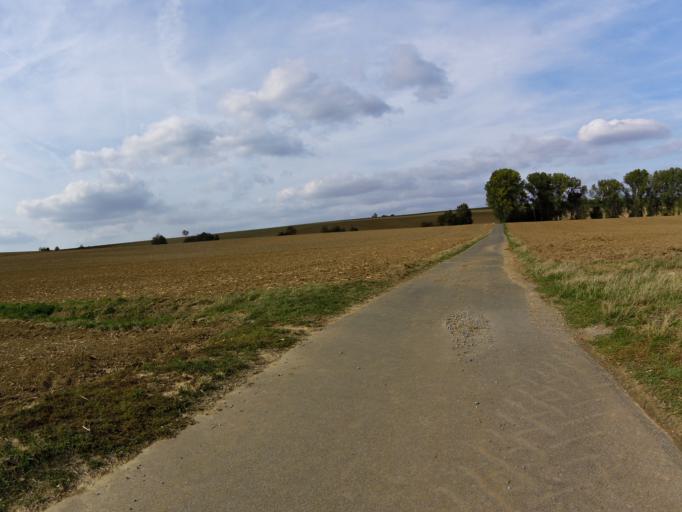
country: DE
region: Bavaria
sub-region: Regierungsbezirk Unterfranken
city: Reichenberg
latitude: 49.7051
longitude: 9.9493
